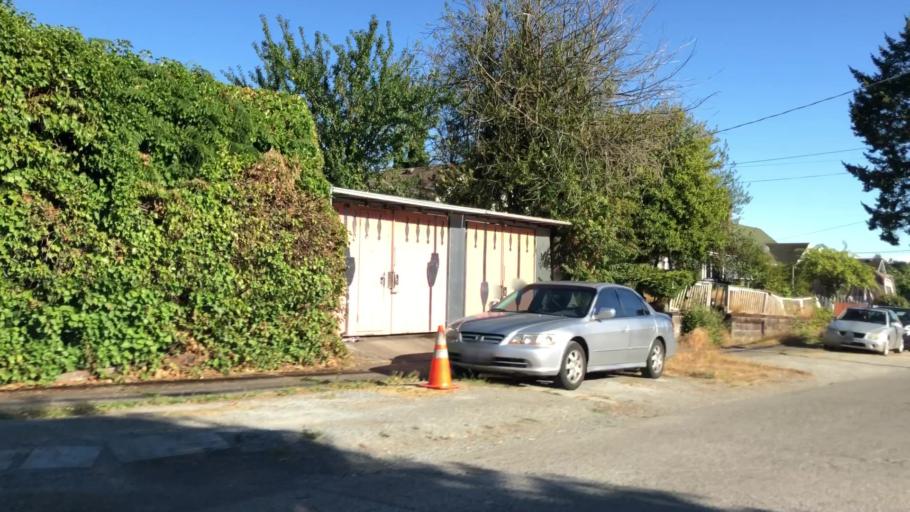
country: US
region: Washington
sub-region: King County
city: Seattle
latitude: 47.5535
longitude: -122.2916
